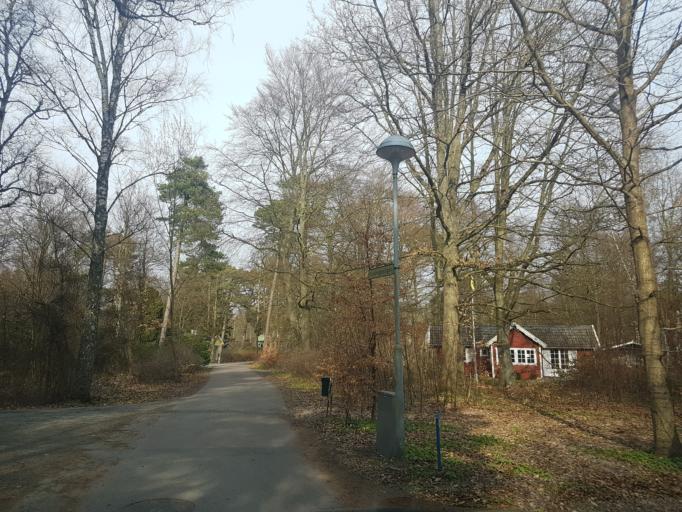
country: SE
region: Skane
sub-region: Ystads Kommun
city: Ystad
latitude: 55.4287
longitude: 13.8531
